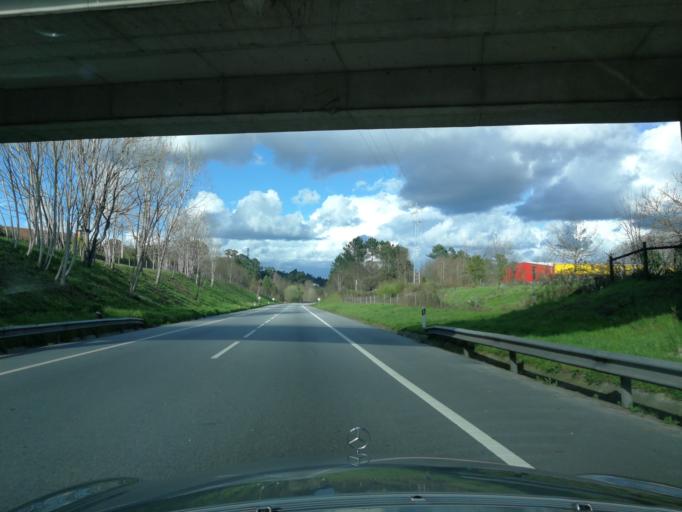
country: PT
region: Braga
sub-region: Vila Verde
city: Prado
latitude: 41.6132
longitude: -8.4536
